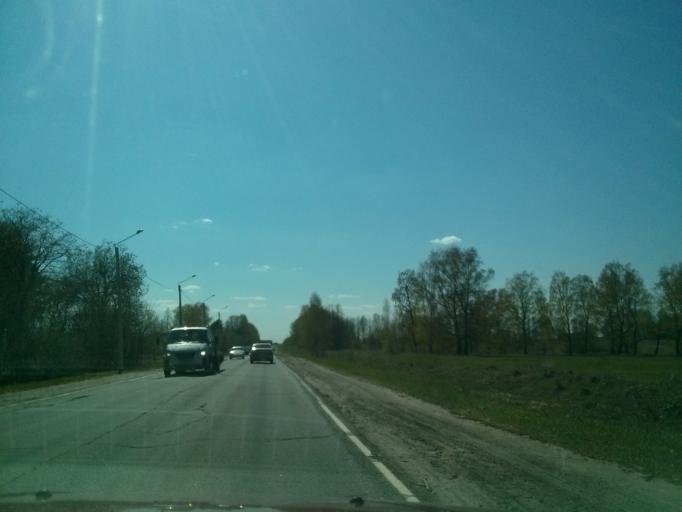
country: RU
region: Nizjnij Novgorod
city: Bogorodsk
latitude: 56.0614
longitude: 43.4199
